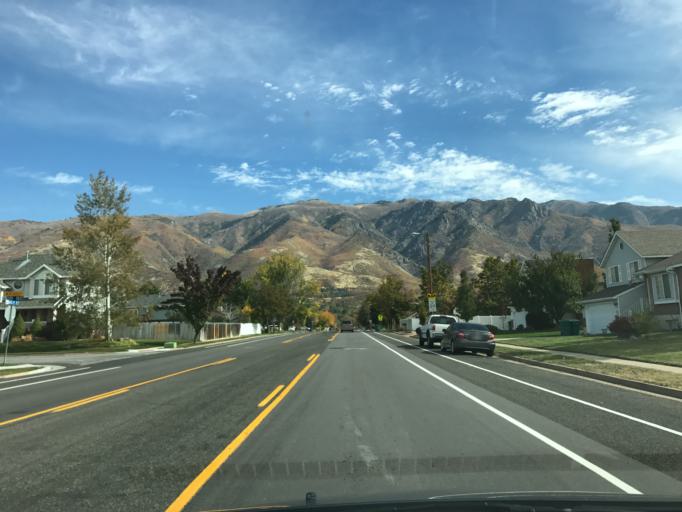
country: US
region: Utah
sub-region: Davis County
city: South Weber
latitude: 41.0891
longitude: -111.9273
